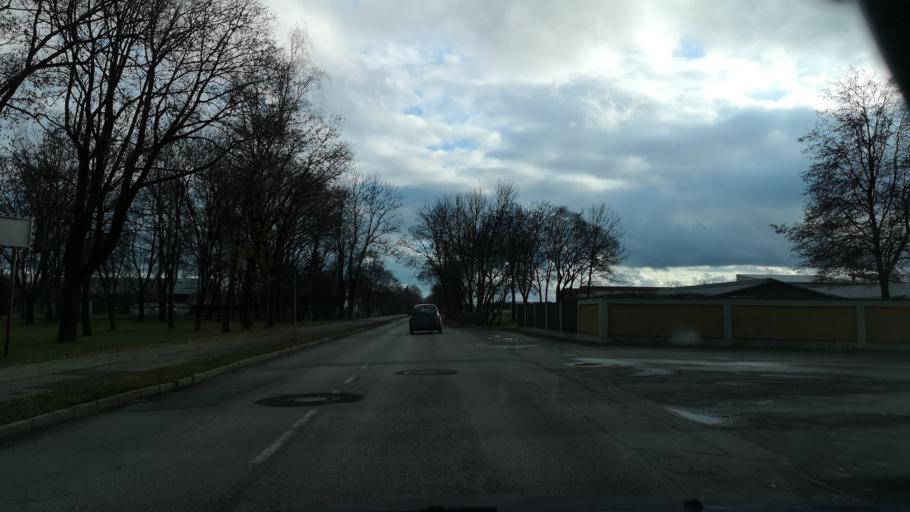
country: DE
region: Bavaria
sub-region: Upper Bavaria
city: Kirchheim bei Muenchen
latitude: 48.1703
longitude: 11.7792
